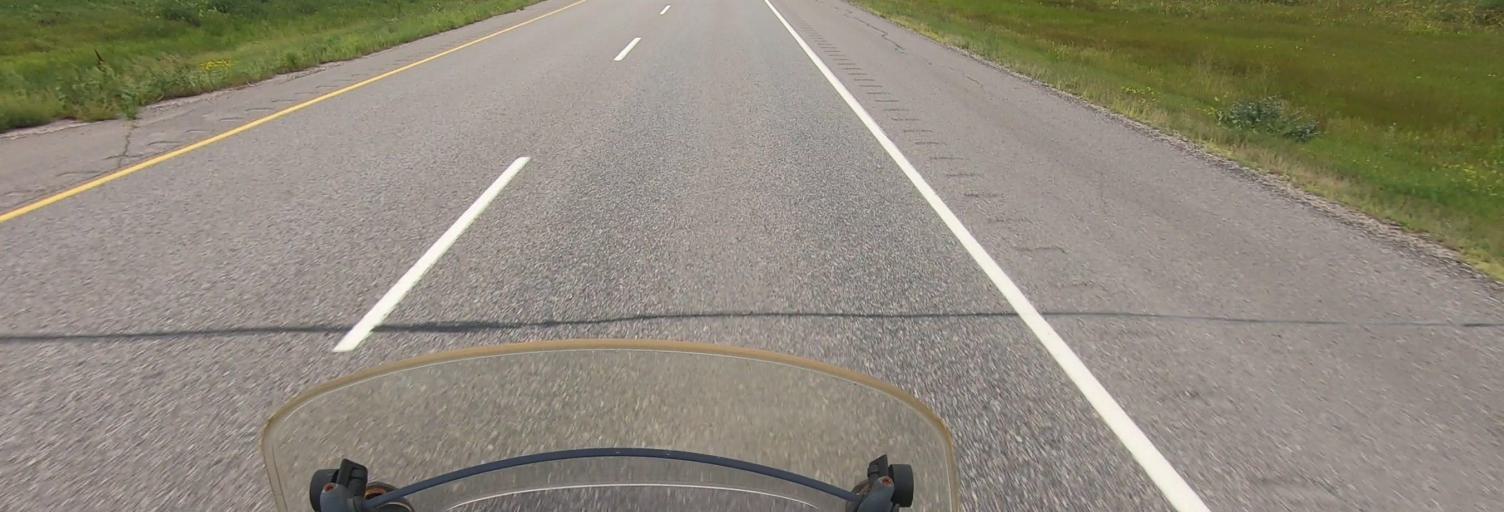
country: CA
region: Manitoba
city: Portage la Prairie
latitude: 49.9755
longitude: -98.6984
